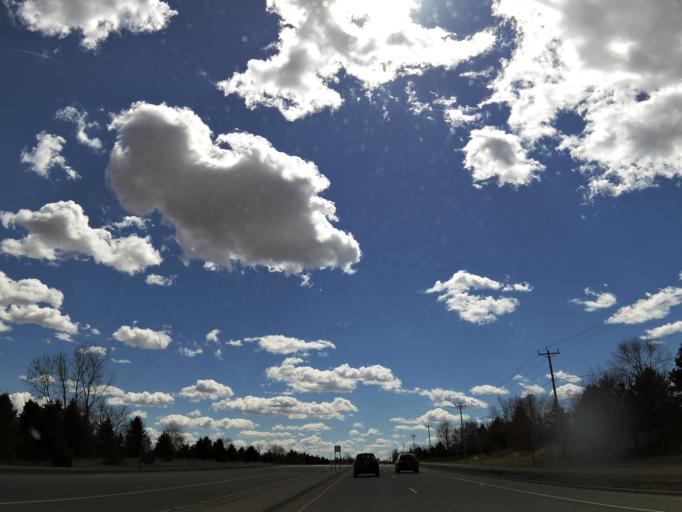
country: US
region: Minnesota
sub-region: Washington County
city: Woodbury
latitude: 44.8966
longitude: -92.9441
